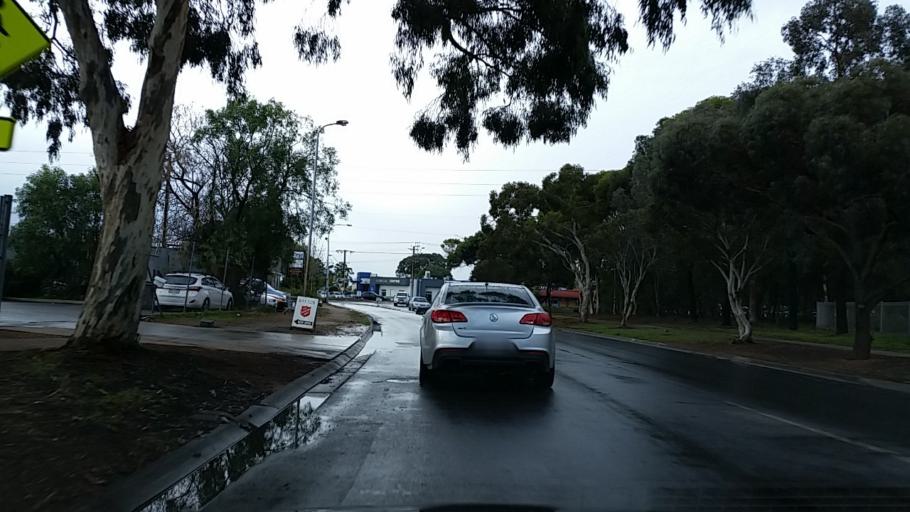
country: AU
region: South Australia
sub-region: Playford
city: Smithfield
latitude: -34.6830
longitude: 138.6883
